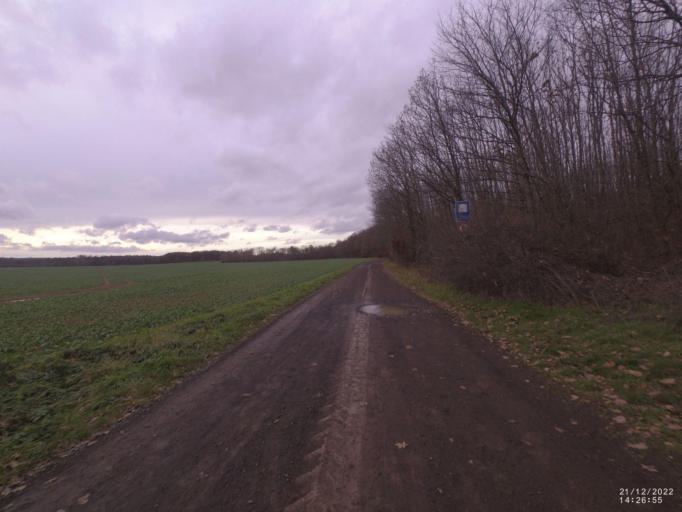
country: DE
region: Rheinland-Pfalz
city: Bad Breisig
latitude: 50.5113
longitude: 7.2664
